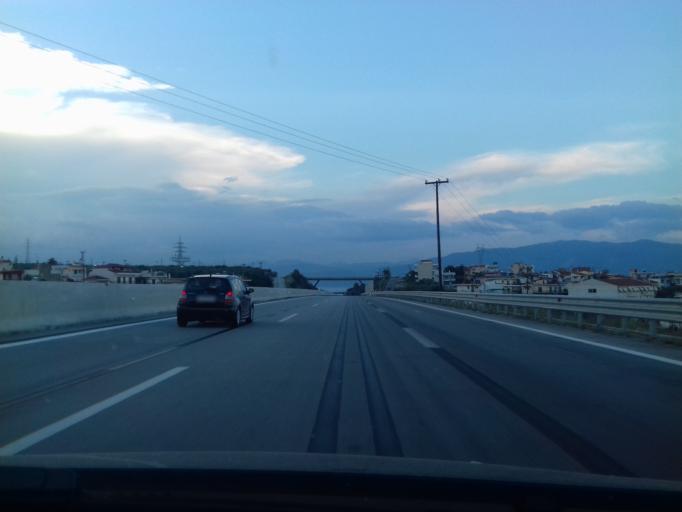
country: GR
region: West Greece
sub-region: Nomos Achaias
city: Aigio
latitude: 38.2447
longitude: 22.0732
